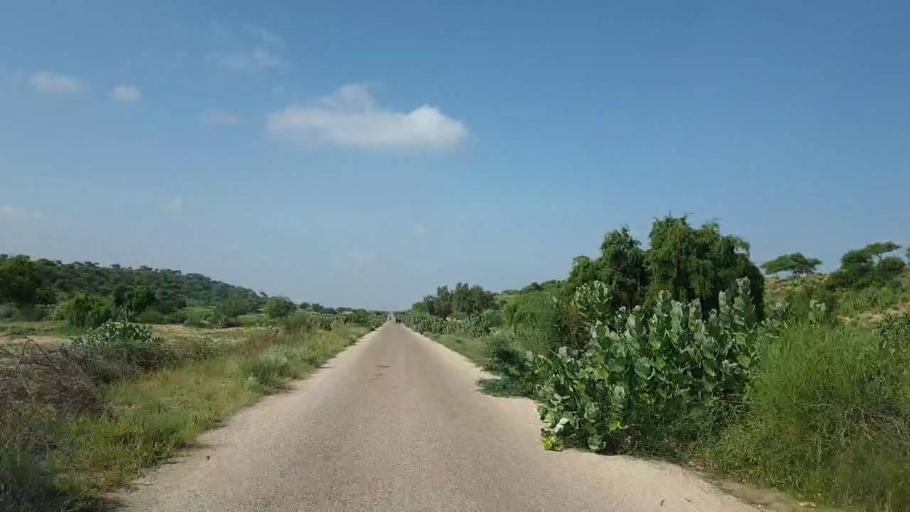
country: PK
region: Sindh
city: Mithi
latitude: 24.5420
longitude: 69.8696
